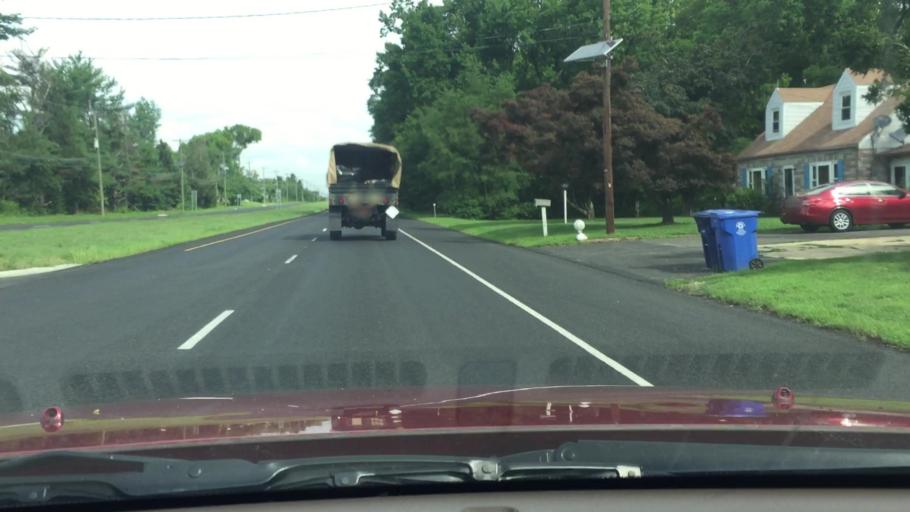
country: US
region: New Jersey
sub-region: Burlington County
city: Bordentown
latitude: 40.1014
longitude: -74.6905
